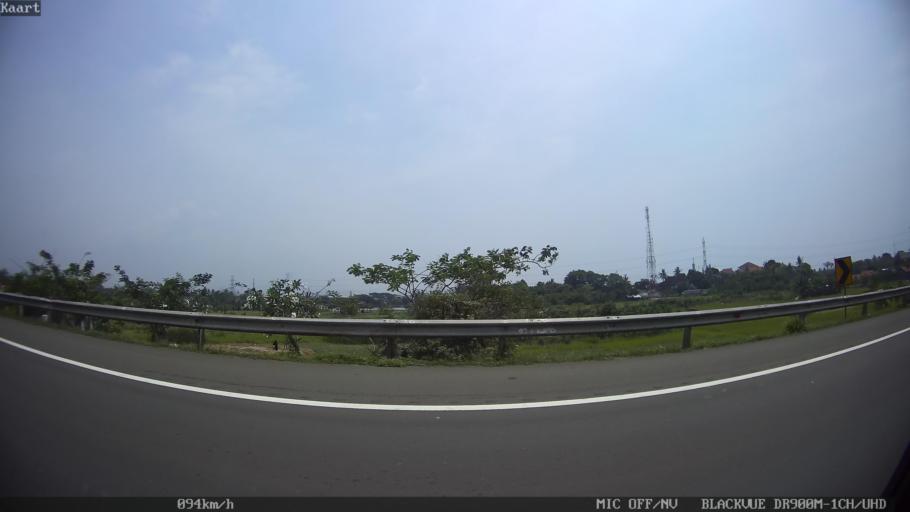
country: ID
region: Banten
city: Curug
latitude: -5.9776
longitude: 106.0124
